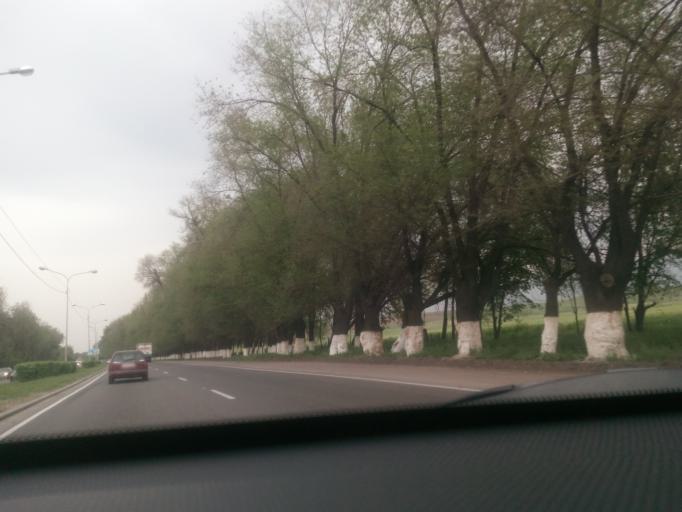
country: KZ
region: Almaty Oblysy
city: Burunday
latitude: 43.2176
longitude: 76.7044
